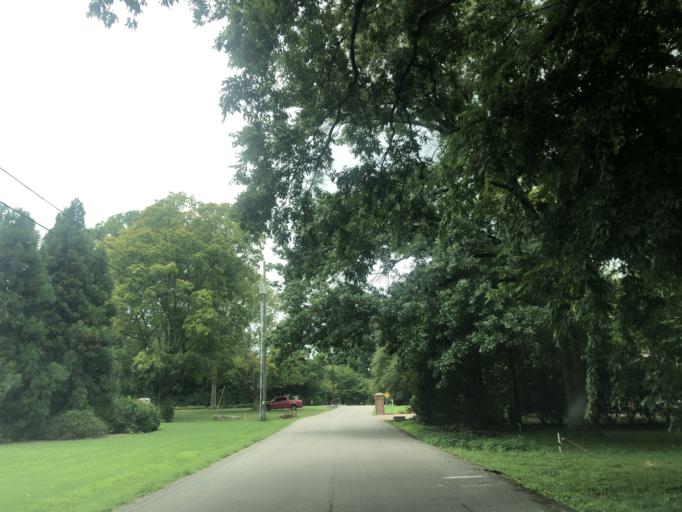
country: US
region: Tennessee
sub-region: Davidson County
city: Oak Hill
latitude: 36.0859
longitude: -86.7938
